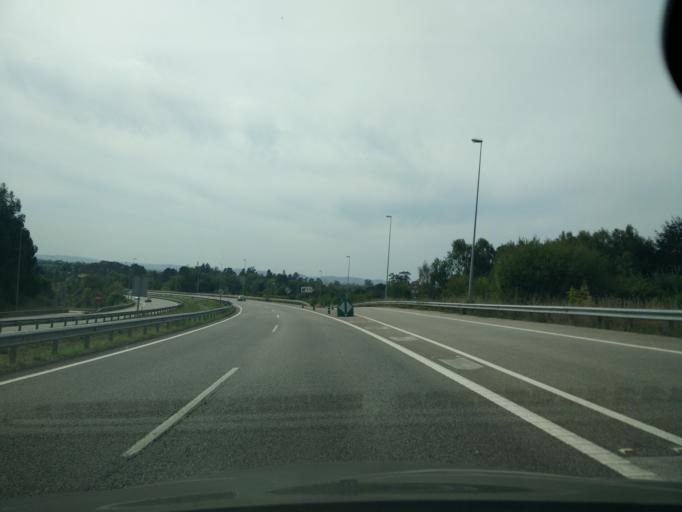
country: ES
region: Asturias
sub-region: Province of Asturias
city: Arriba
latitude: 43.5107
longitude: -5.5983
